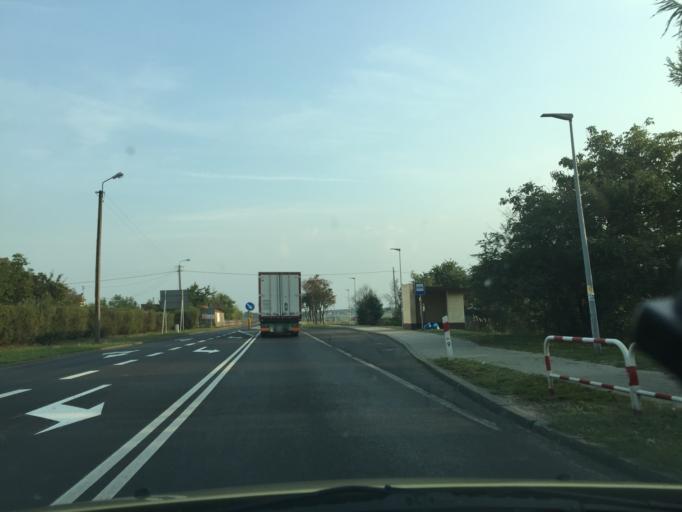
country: PL
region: Greater Poland Voivodeship
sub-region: Powiat jarocinski
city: Jarocin
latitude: 52.0232
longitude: 17.4645
